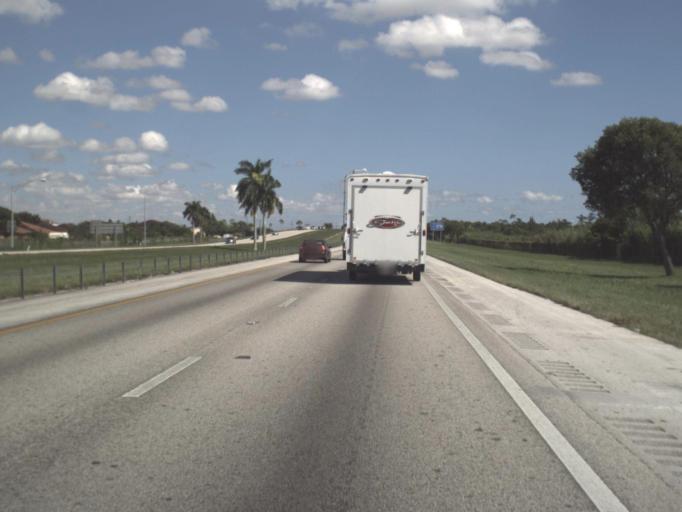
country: US
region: Florida
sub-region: Miami-Dade County
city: Naranja
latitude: 25.5140
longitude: -80.4084
